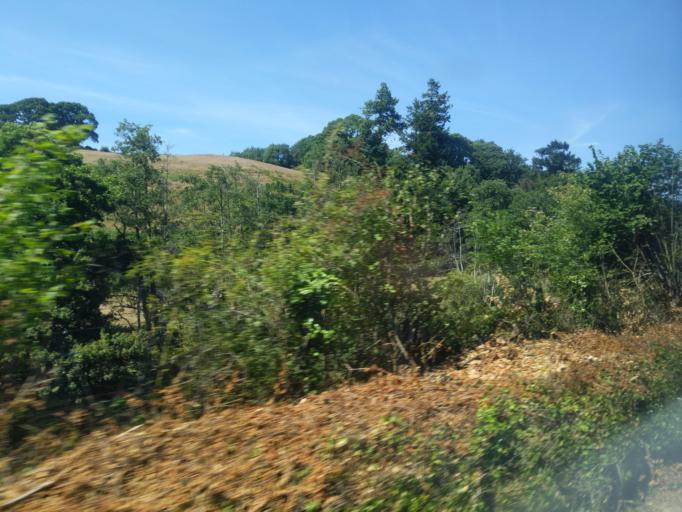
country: GB
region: England
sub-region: Devon
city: Totnes
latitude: 50.4547
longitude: -3.6717
